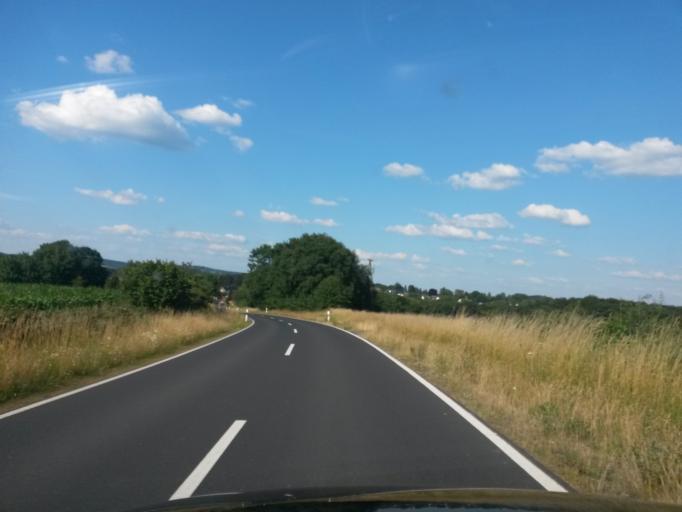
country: DE
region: North Rhine-Westphalia
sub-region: Regierungsbezirk Koln
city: Much
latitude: 50.9047
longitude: 7.3575
